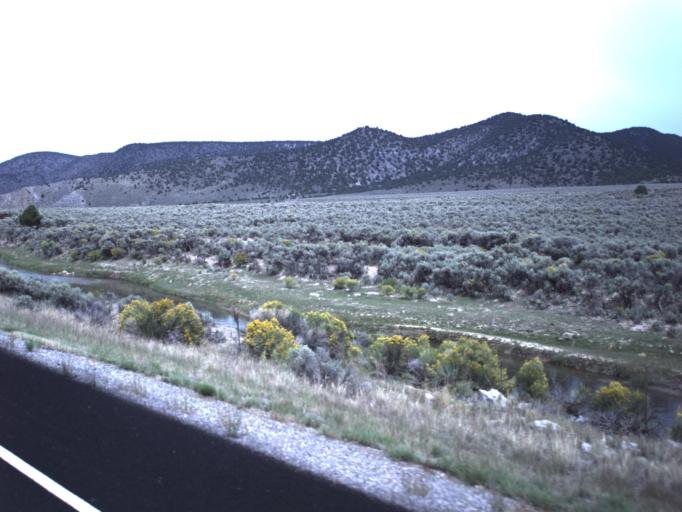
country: US
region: Utah
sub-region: Piute County
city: Junction
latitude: 38.0486
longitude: -112.3535
